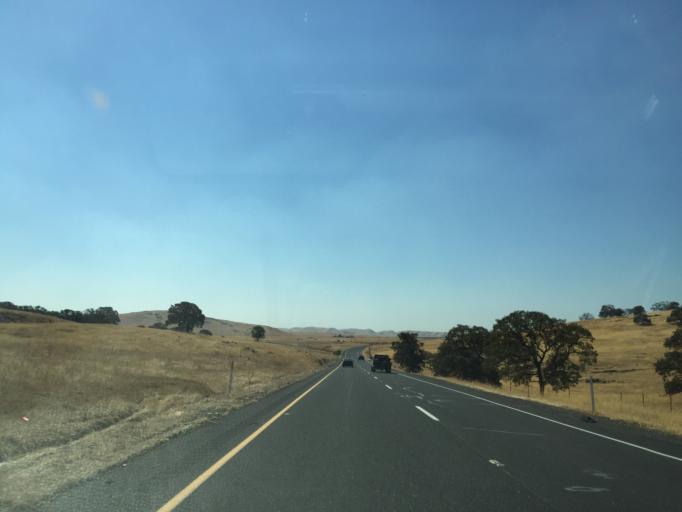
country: US
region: California
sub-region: Calaveras County
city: Copperopolis
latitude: 37.8372
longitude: -120.6271
